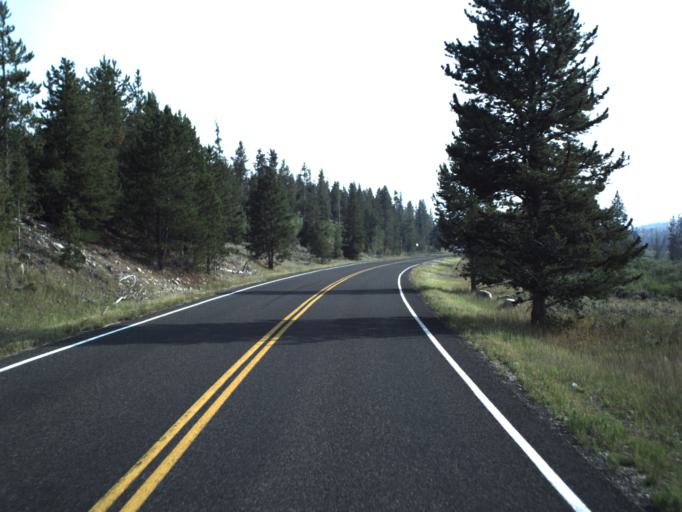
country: US
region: Wyoming
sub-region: Uinta County
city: Evanston
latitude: 40.8889
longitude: -110.8315
